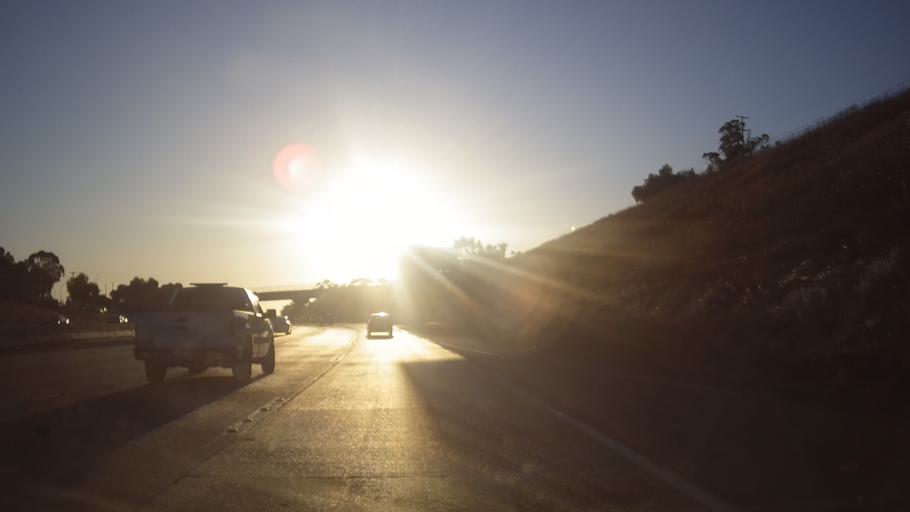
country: US
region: California
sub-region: San Diego County
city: Lemon Grove
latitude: 32.7474
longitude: -117.0281
